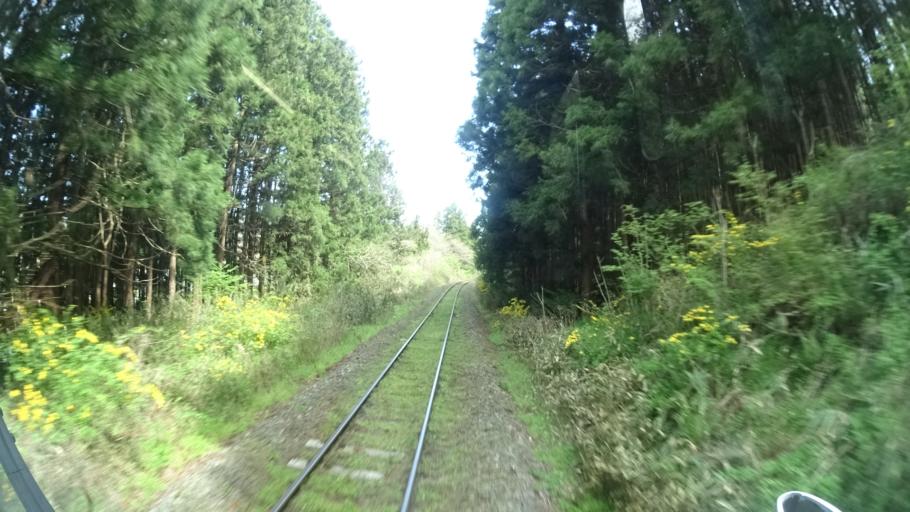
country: JP
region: Iwate
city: Ichinoseki
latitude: 38.9927
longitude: 141.2564
